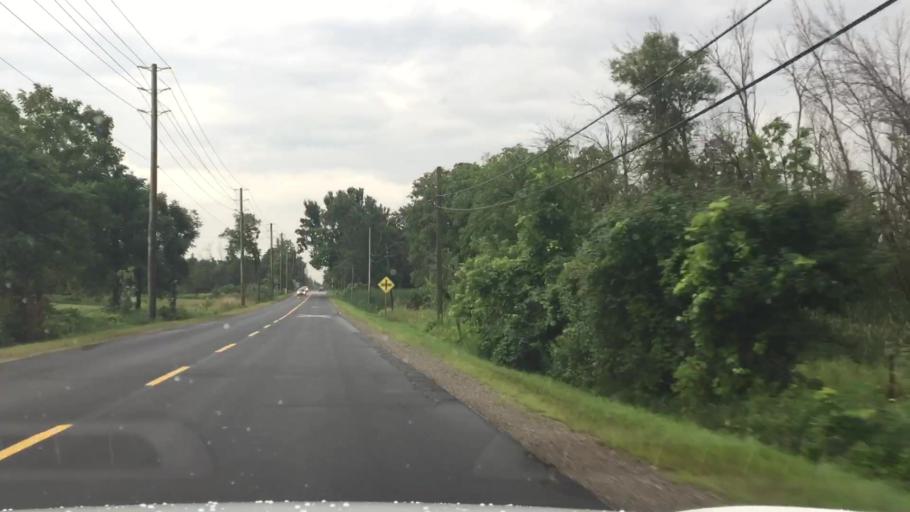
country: CA
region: Ontario
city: Markham
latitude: 43.8746
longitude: -79.2082
